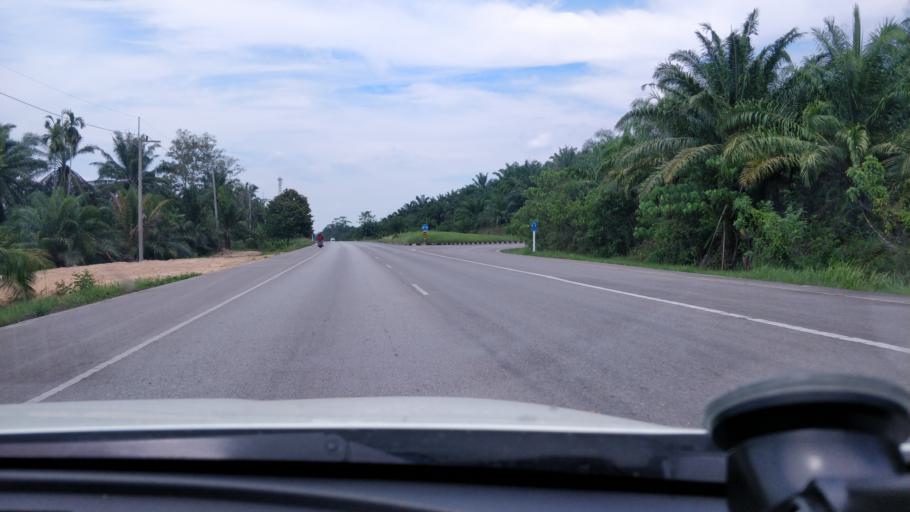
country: TH
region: Krabi
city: Plai Phraya
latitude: 8.4432
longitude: 98.8512
